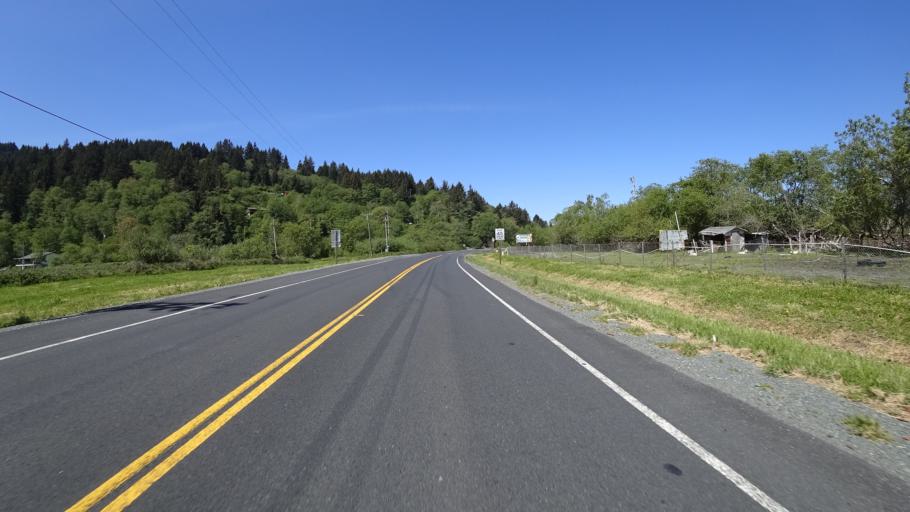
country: US
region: California
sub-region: Humboldt County
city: Westhaven-Moonstone
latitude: 41.2847
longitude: -124.0747
